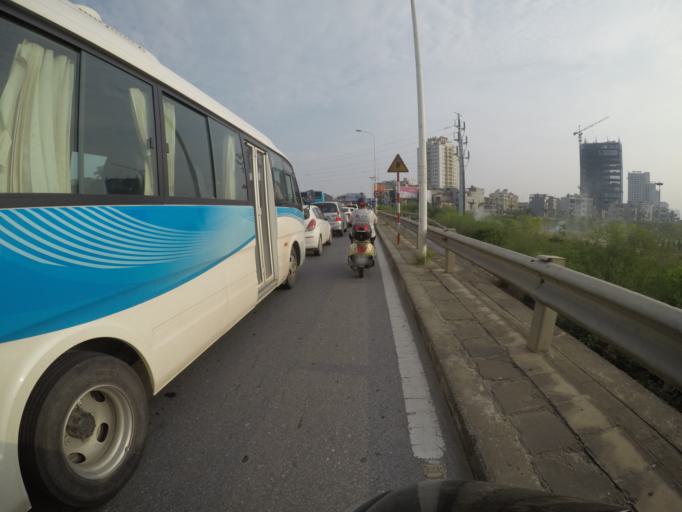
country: VN
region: Ha Noi
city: Tay Ho
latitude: 21.0834
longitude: 105.8169
